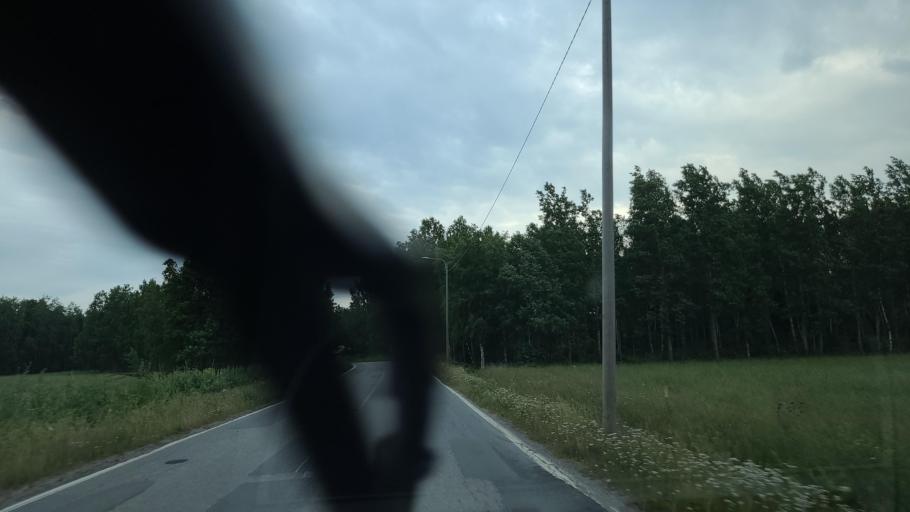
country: FI
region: Ostrobothnia
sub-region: Vaasa
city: Replot
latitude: 63.1874
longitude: 21.2995
